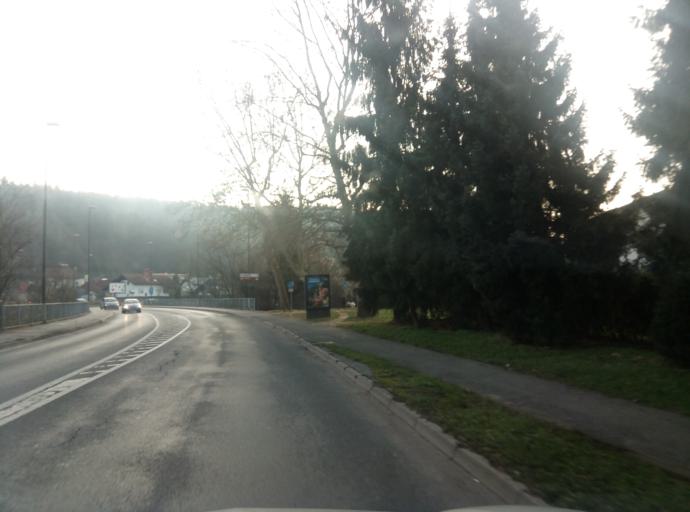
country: SI
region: Ljubljana
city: Ljubljana
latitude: 46.0504
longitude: 14.5389
